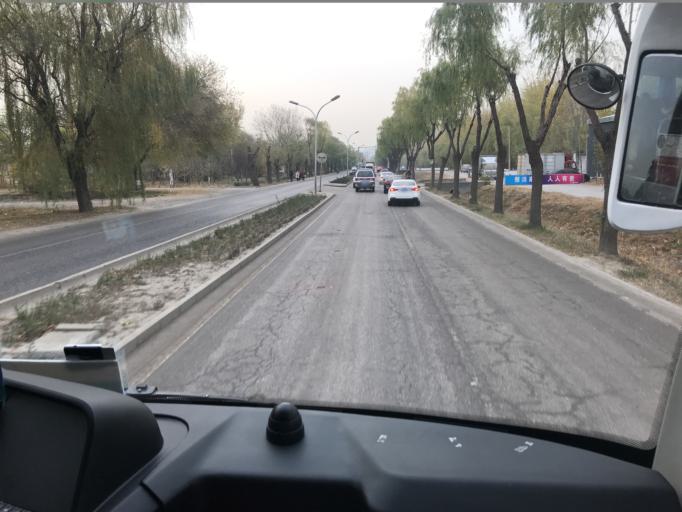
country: CN
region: Beijing
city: Wenquan
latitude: 40.0881
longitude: 116.2100
